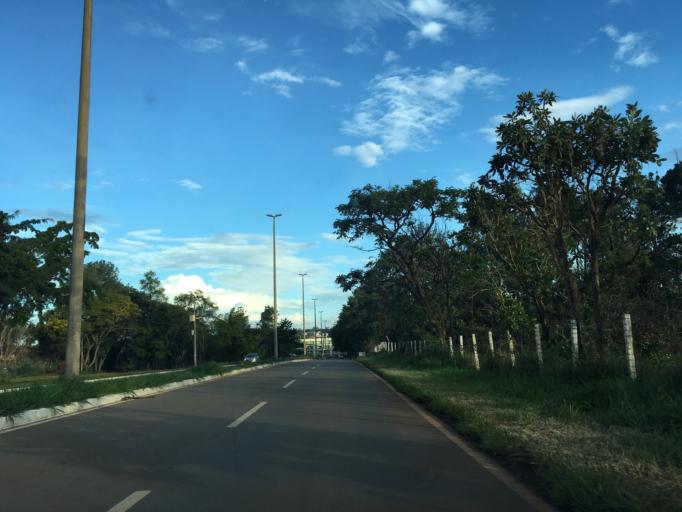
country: BR
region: Federal District
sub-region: Brasilia
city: Brasilia
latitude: -15.8048
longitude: -47.8342
